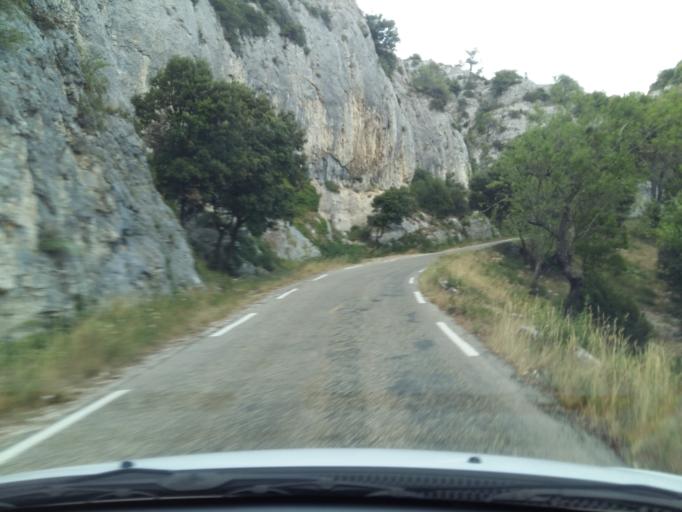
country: FR
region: Provence-Alpes-Cote d'Azur
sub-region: Departement du Vaucluse
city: Venasque
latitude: 43.9853
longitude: 5.1872
